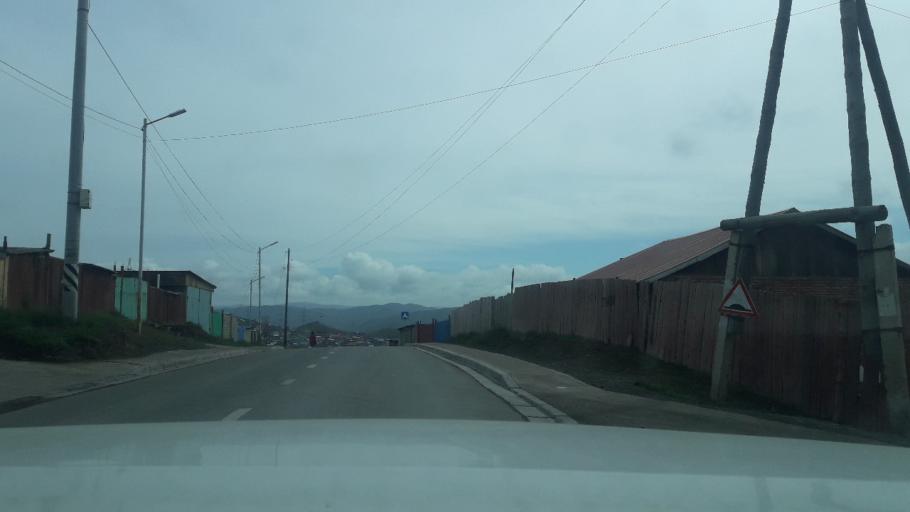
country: MN
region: Ulaanbaatar
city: Ulaanbaatar
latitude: 47.9654
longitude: 106.8792
